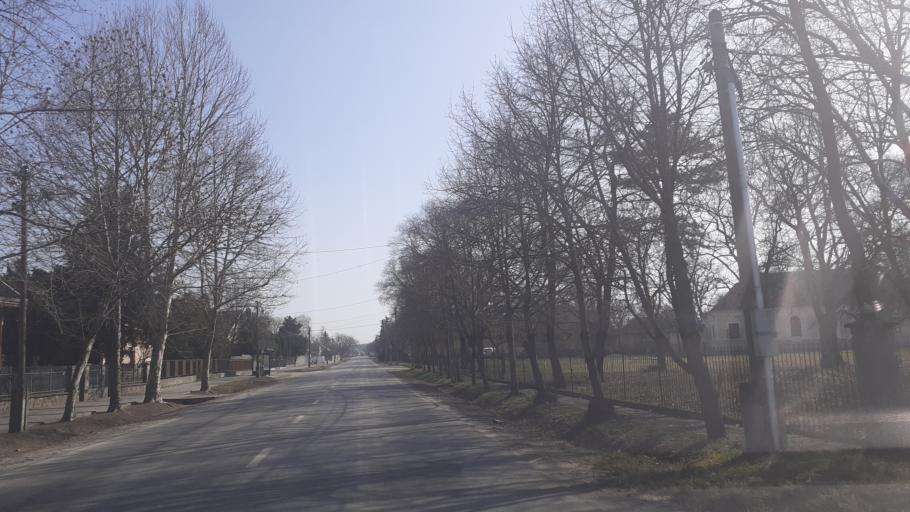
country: HU
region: Pest
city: Dabas
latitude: 47.1669
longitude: 19.3279
